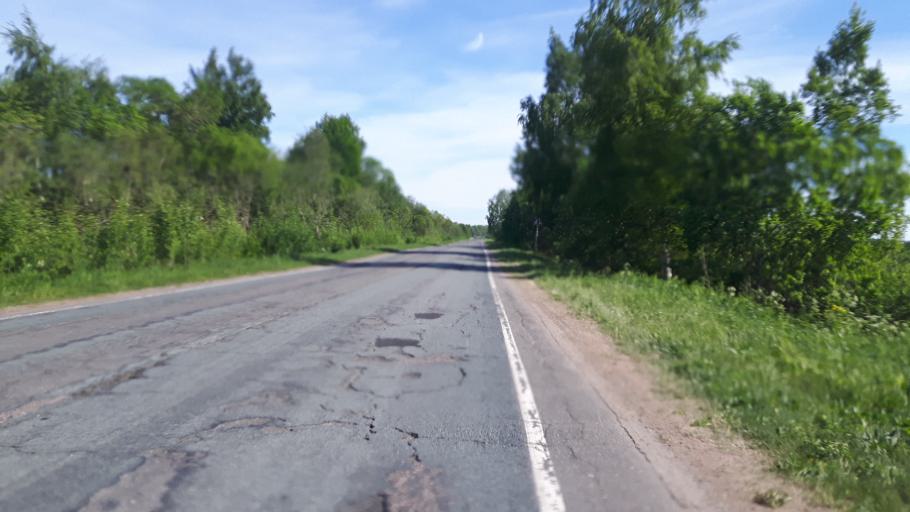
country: RU
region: Leningrad
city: Ivangorod
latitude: 59.4210
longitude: 28.3203
